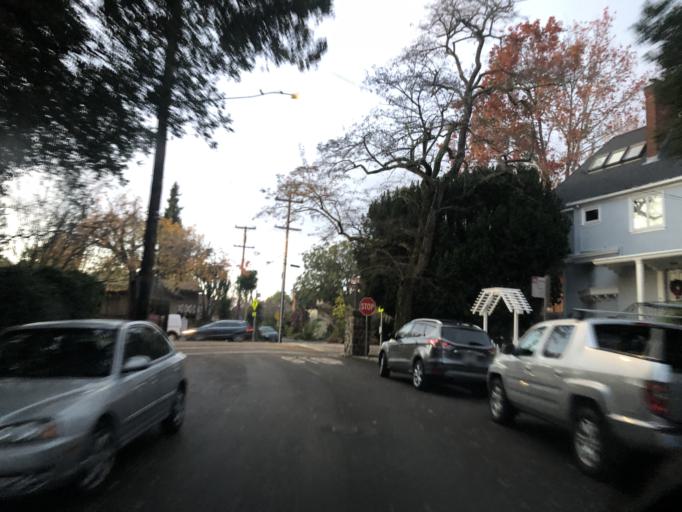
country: US
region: California
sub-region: Alameda County
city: Berkeley
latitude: 37.8527
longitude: -122.2492
